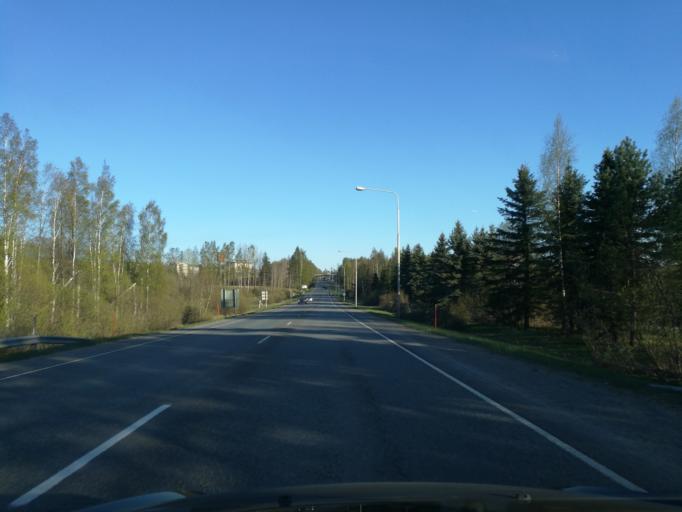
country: FI
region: Uusimaa
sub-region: Helsinki
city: Tuusula
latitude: 60.4018
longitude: 25.0115
